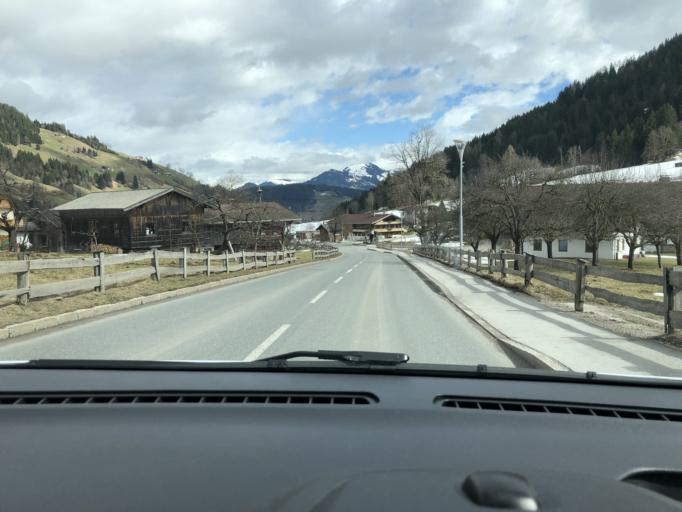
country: AT
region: Tyrol
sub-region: Politischer Bezirk Kufstein
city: Worgl
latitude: 47.4454
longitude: 12.0534
